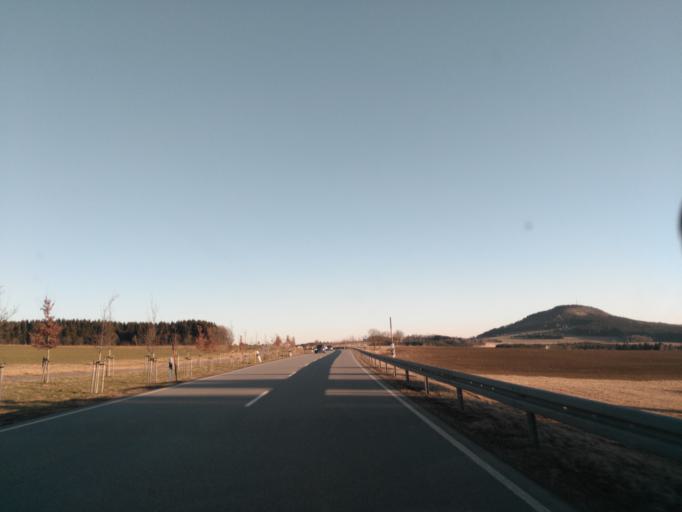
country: DE
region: Saxony
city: Konigswalde
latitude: 50.5331
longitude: 13.0257
